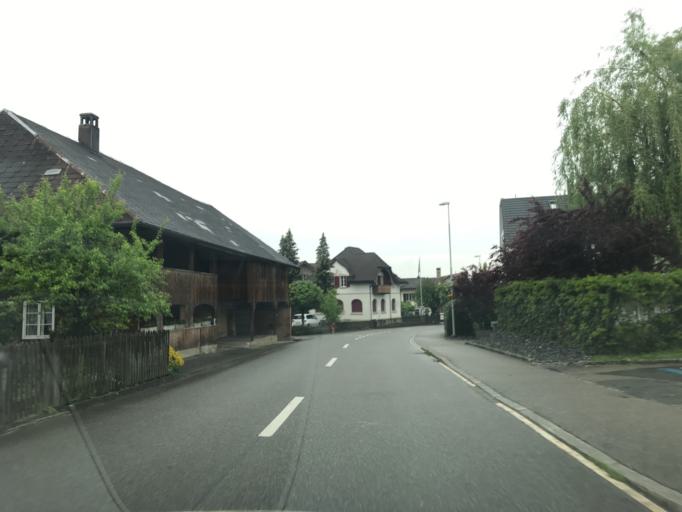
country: CH
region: Bern
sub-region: Oberaargau
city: Langenthal
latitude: 47.2080
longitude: 7.7750
